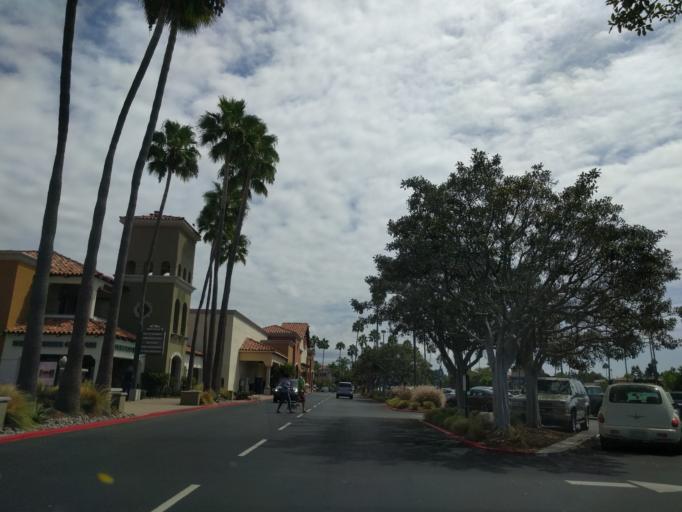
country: US
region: California
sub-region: San Diego County
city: Encinitas
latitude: 33.1016
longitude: -117.3115
